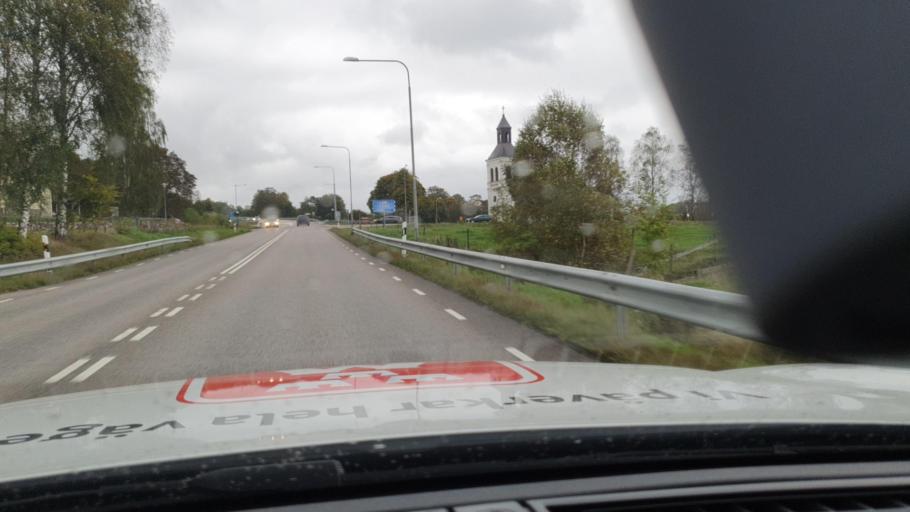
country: SE
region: Halland
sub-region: Falkenbergs Kommun
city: Falkenberg
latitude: 56.9895
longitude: 12.5836
